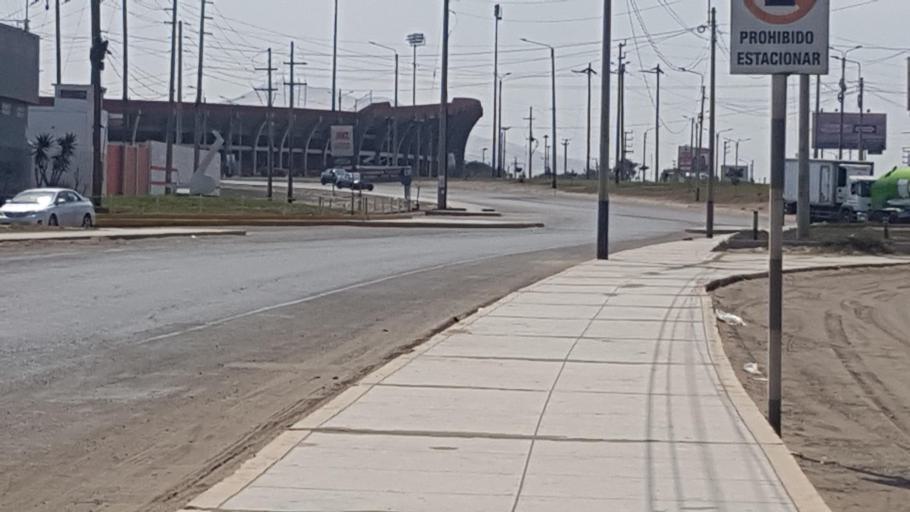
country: PE
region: Ancash
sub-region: Provincia de Santa
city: Chimbote
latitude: -9.1047
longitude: -78.5594
